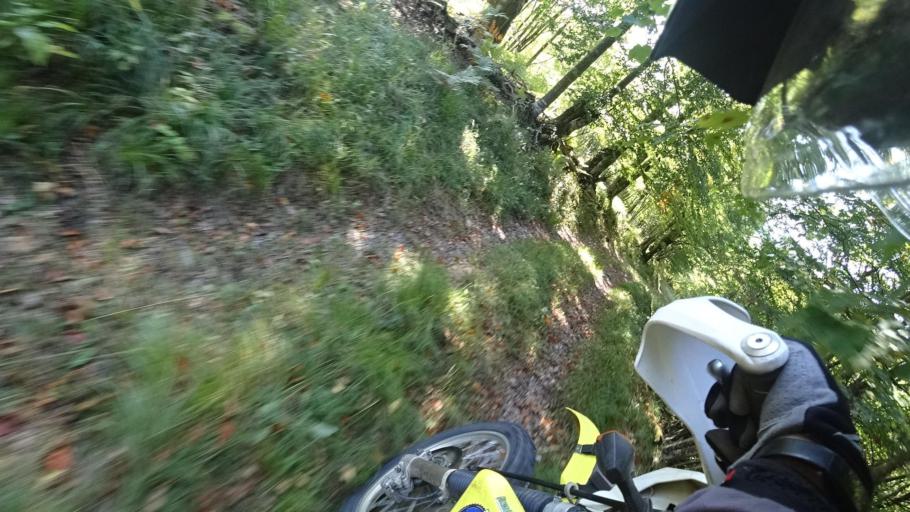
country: HR
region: Karlovacka
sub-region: Grad Ogulin
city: Ogulin
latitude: 45.1927
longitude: 15.1281
